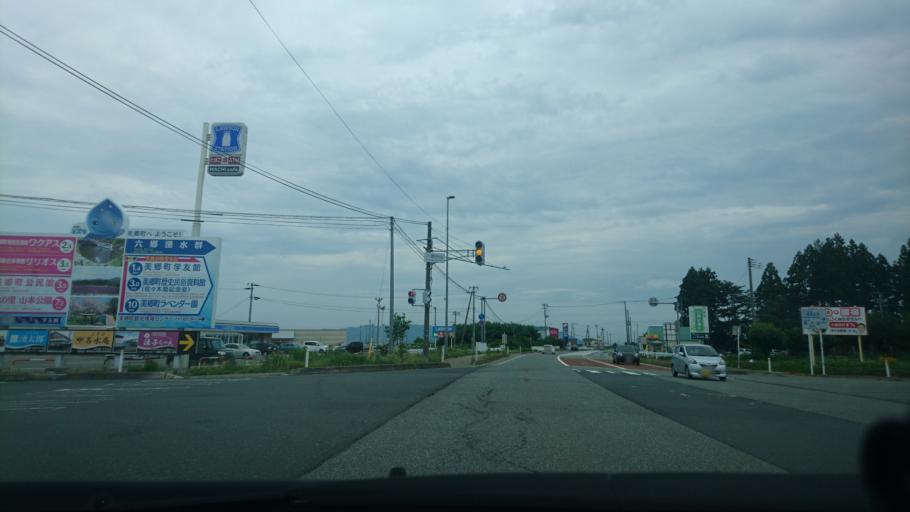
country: JP
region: Akita
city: Omagari
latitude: 39.4165
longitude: 140.5436
